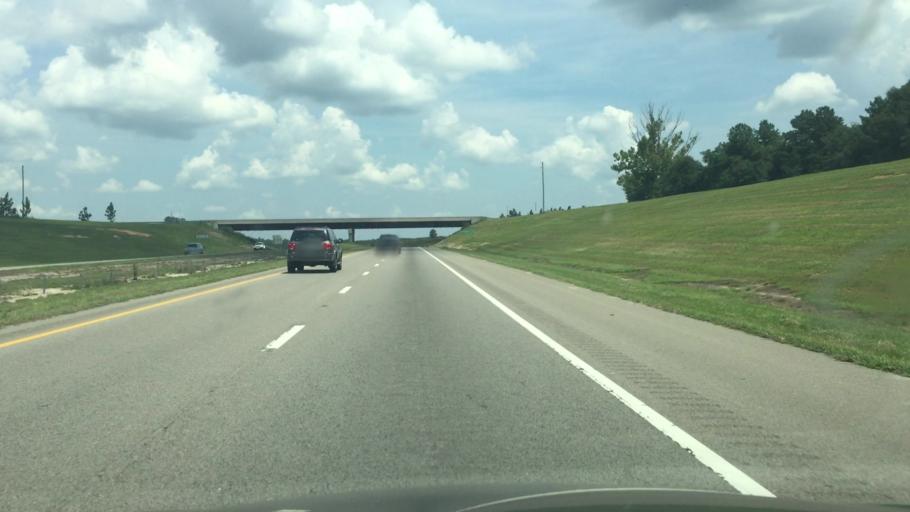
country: US
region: North Carolina
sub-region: Richmond County
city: Ellerbe
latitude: 35.1713
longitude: -79.7142
